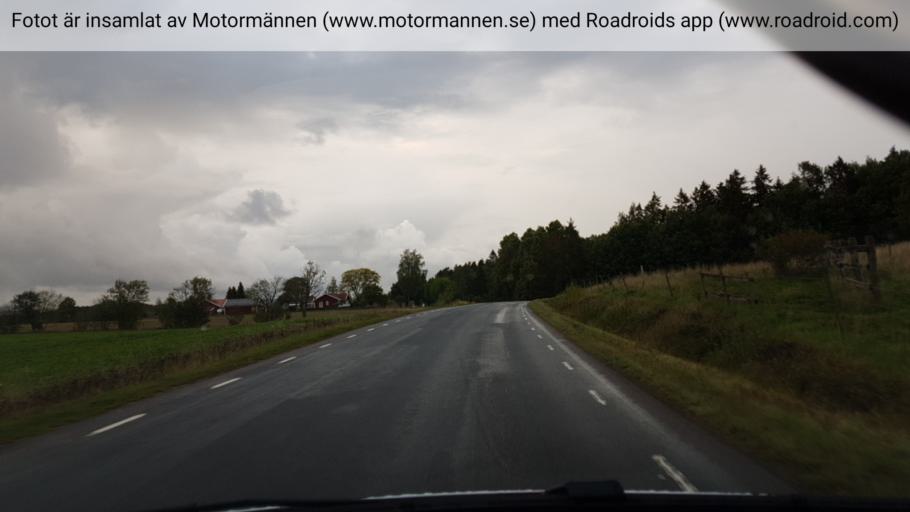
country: SE
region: Vaestra Goetaland
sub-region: Skovde Kommun
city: Skoevde
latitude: 58.3637
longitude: 13.9473
